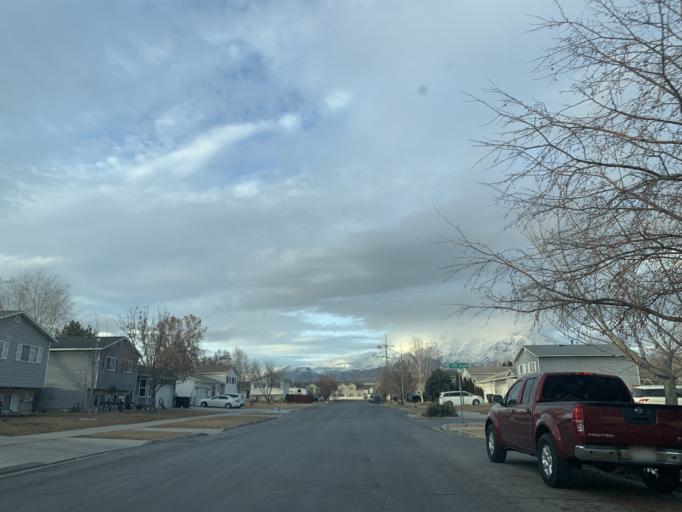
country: US
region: Utah
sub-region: Utah County
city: Provo
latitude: 40.2272
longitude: -111.6826
